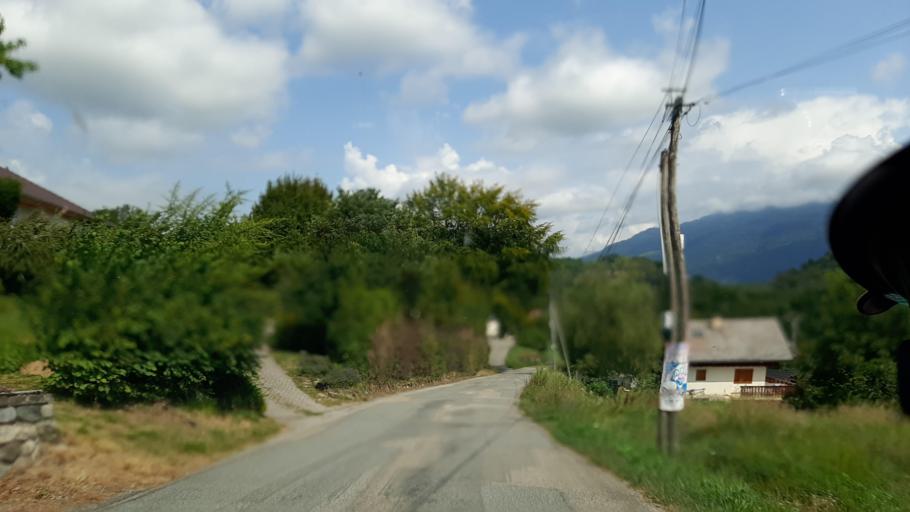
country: FR
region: Rhone-Alpes
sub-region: Departement de la Savoie
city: Mercury
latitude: 45.6863
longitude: 6.3564
